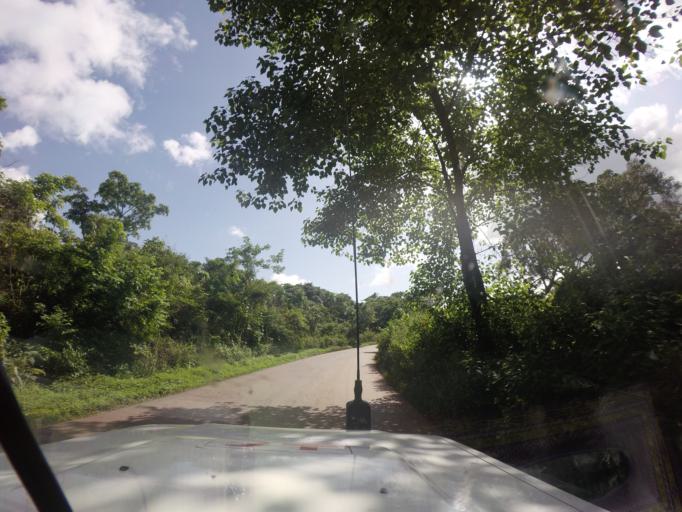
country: GN
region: Mamou
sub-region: Mamou Prefecture
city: Mamou
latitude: 10.3500
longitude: -12.1853
